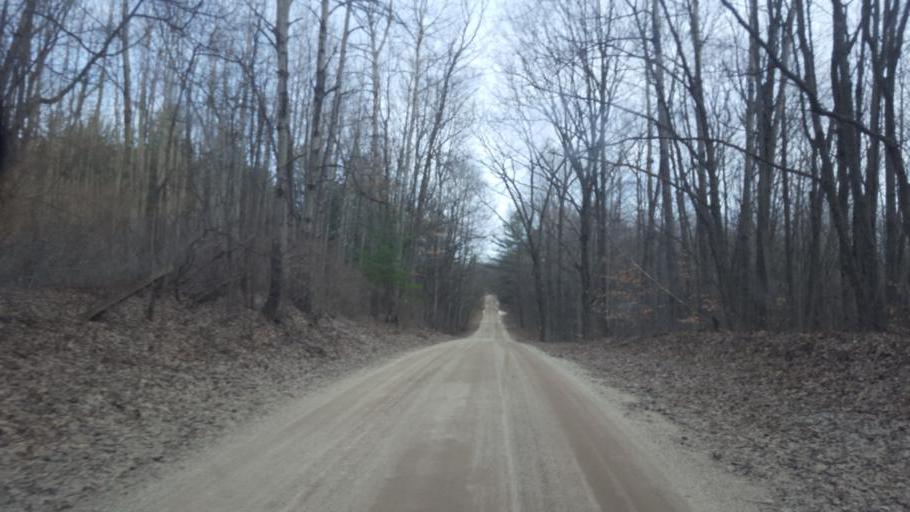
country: US
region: Michigan
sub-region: Isabella County
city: Lake Isabella
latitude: 43.6792
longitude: -85.1318
